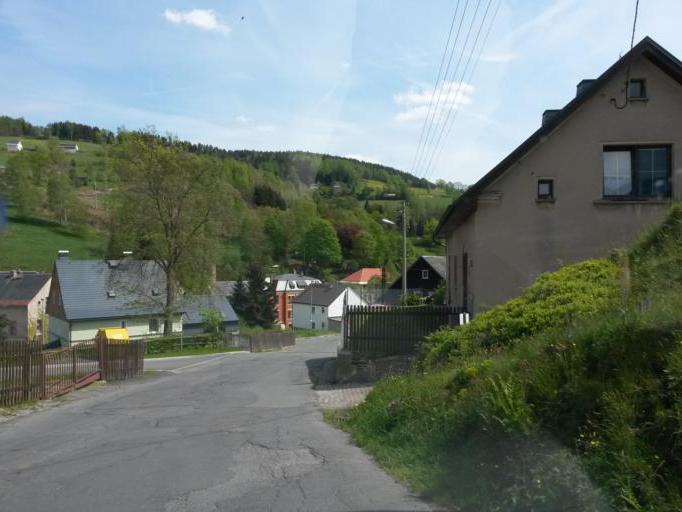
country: DE
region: Saxony
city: Klingenthal
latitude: 50.3709
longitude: 12.4683
